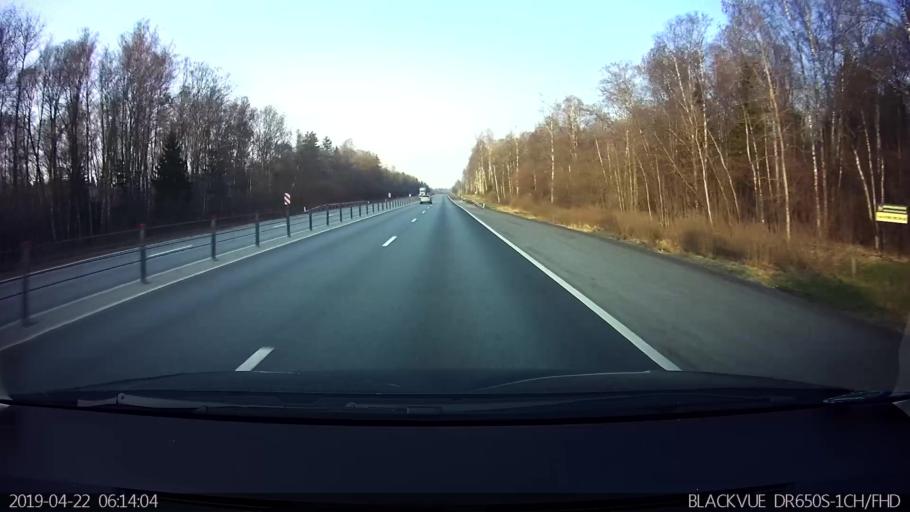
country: RU
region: Moskovskaya
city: Mozhaysk
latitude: 55.4655
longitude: 36.0869
